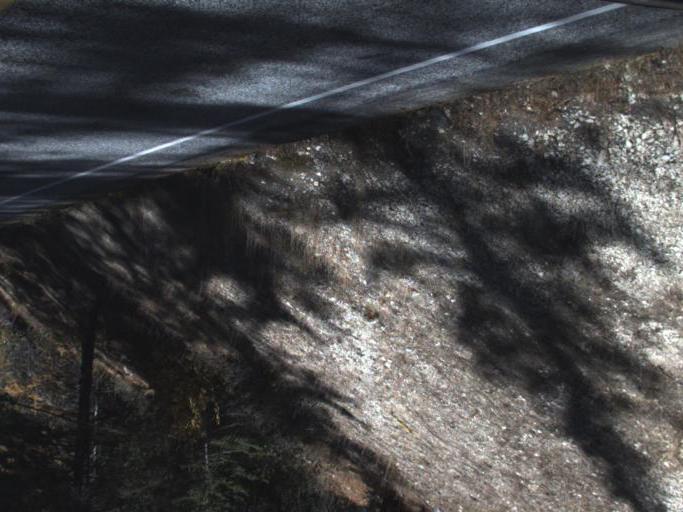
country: US
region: Washington
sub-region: Ferry County
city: Republic
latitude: 48.6103
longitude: -118.4469
